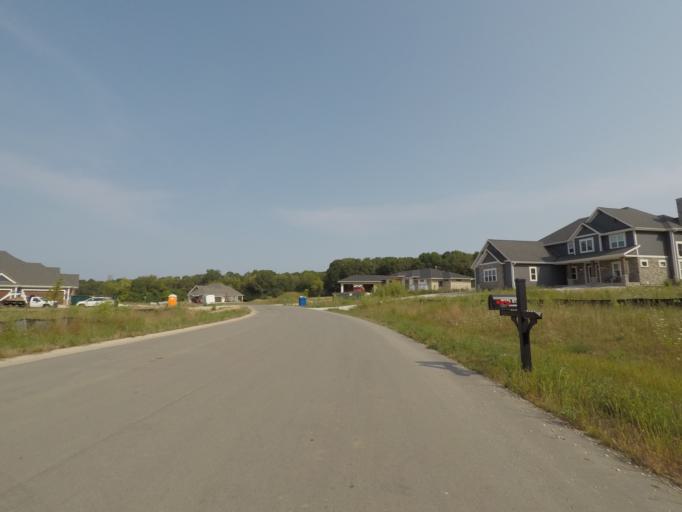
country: US
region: Wisconsin
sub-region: Waukesha County
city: Delafield
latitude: 43.0257
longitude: -88.4167
